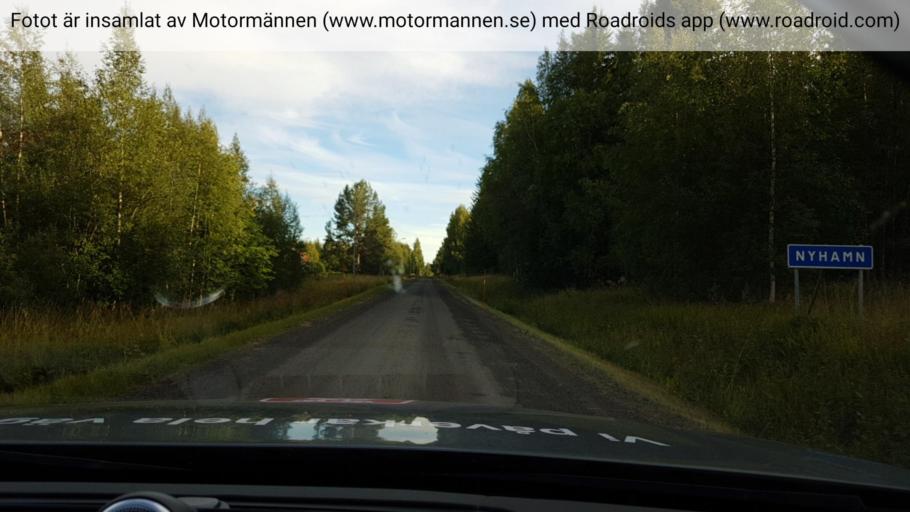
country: SE
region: Jaemtland
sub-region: Stroemsunds Kommun
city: Stroemsund
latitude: 64.1196
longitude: 15.8074
